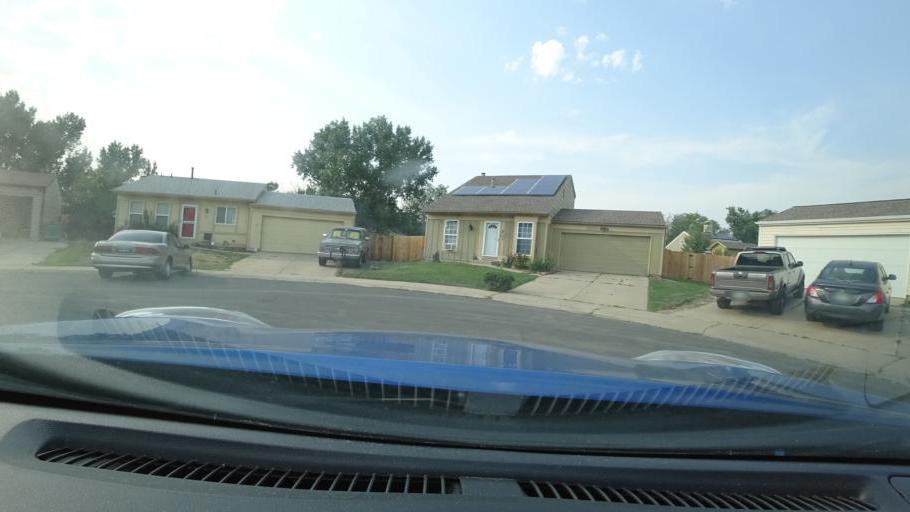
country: US
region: Colorado
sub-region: Adams County
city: Aurora
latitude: 39.7439
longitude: -104.7573
